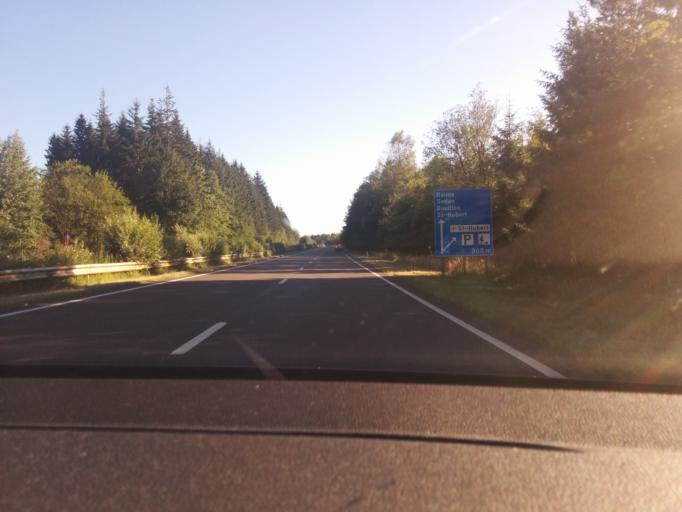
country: BE
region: Wallonia
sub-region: Province du Luxembourg
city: Saint-Hubert
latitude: 50.0549
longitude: 5.4035
